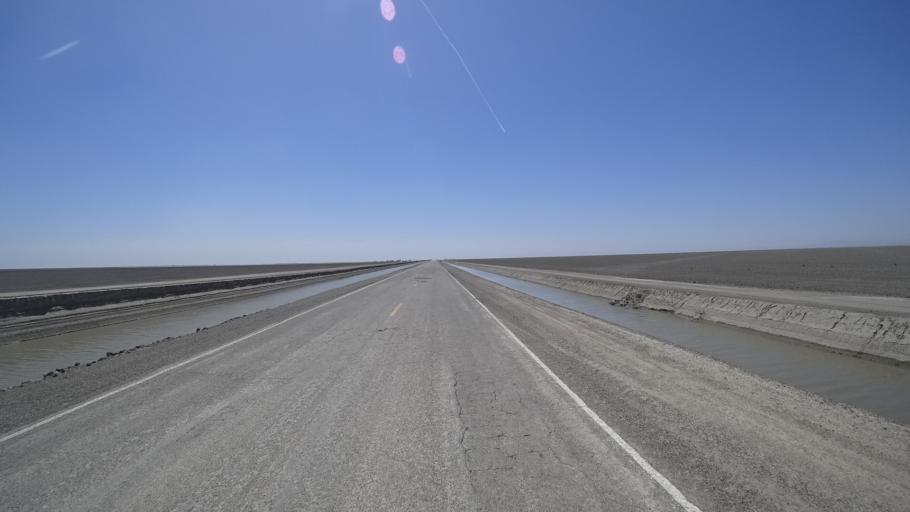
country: US
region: California
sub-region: Kings County
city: Corcoran
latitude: 35.9997
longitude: -119.6433
